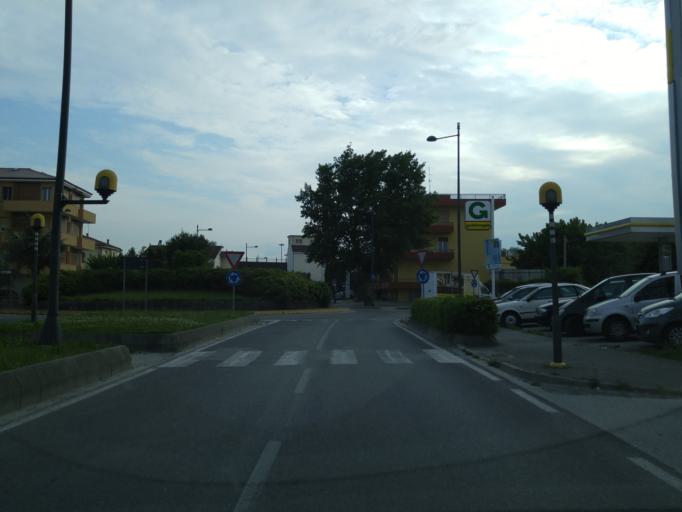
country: IT
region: The Marches
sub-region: Provincia di Ancona
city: Senigallia
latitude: 43.7060
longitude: 13.2101
